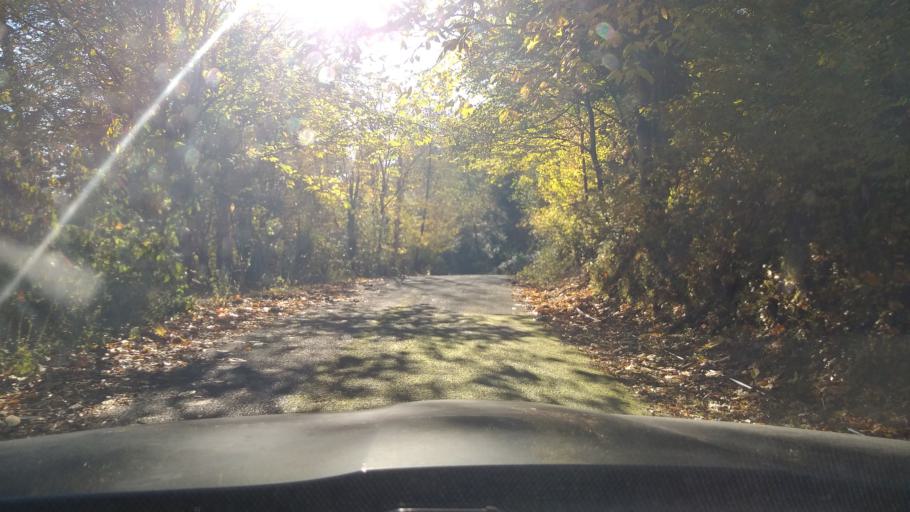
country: GE
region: Abkhazia
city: Bich'vinta
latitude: 43.1837
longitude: 40.4545
